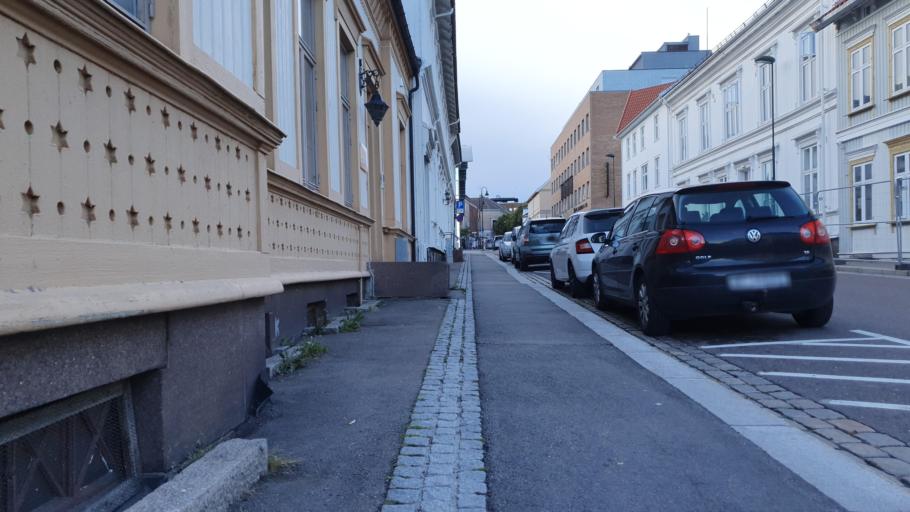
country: NO
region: Vestfold
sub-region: Tonsberg
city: Tonsberg
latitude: 59.2654
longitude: 10.4112
